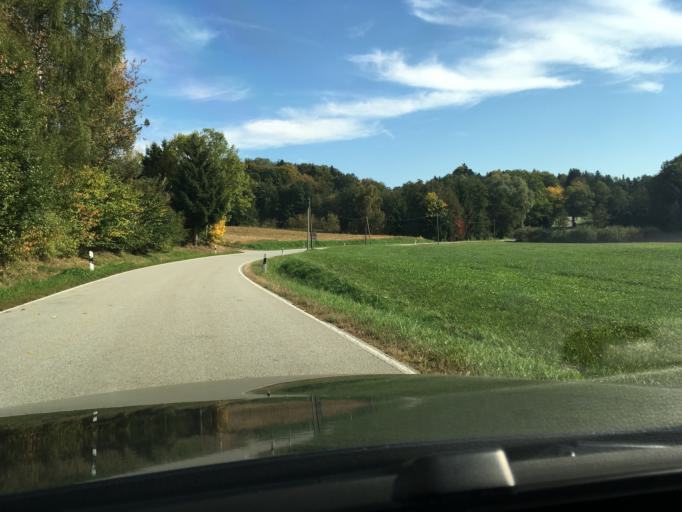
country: DE
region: Bavaria
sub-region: Lower Bavaria
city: Hofkirchen
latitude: 48.6981
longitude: 13.1273
